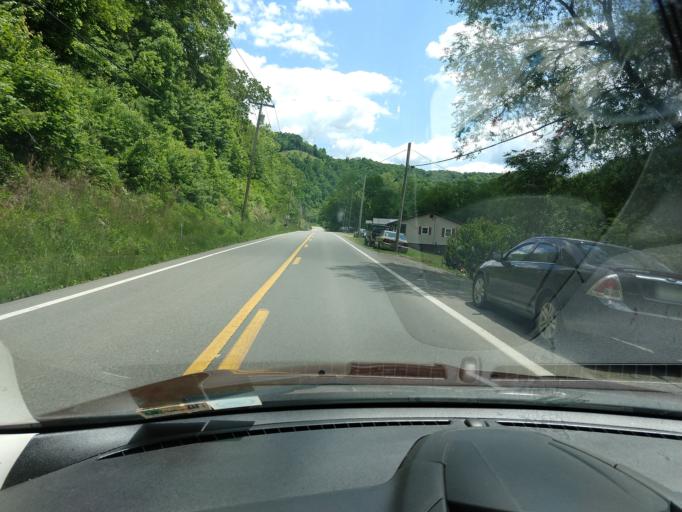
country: US
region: West Virginia
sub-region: Gilmer County
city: Glenville
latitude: 38.8772
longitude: -80.7069
